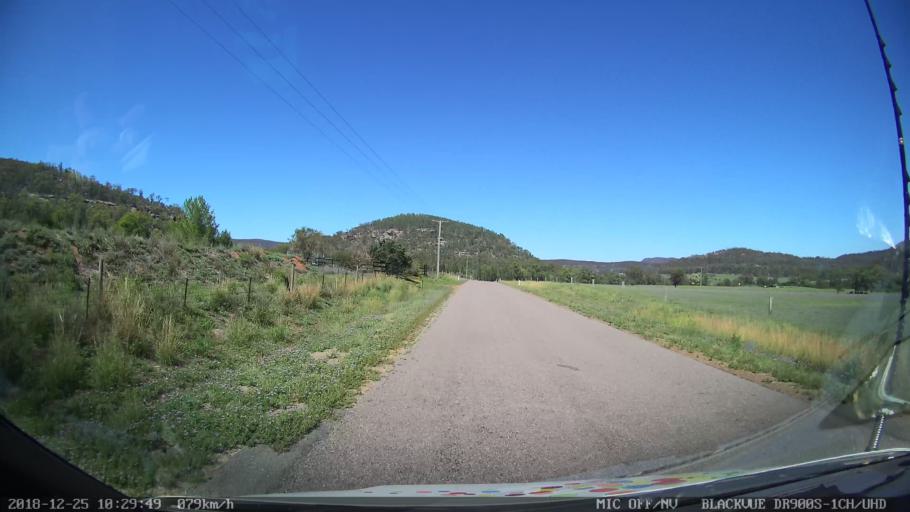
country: AU
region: New South Wales
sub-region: Muswellbrook
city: Denman
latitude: -32.3806
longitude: 150.4461
